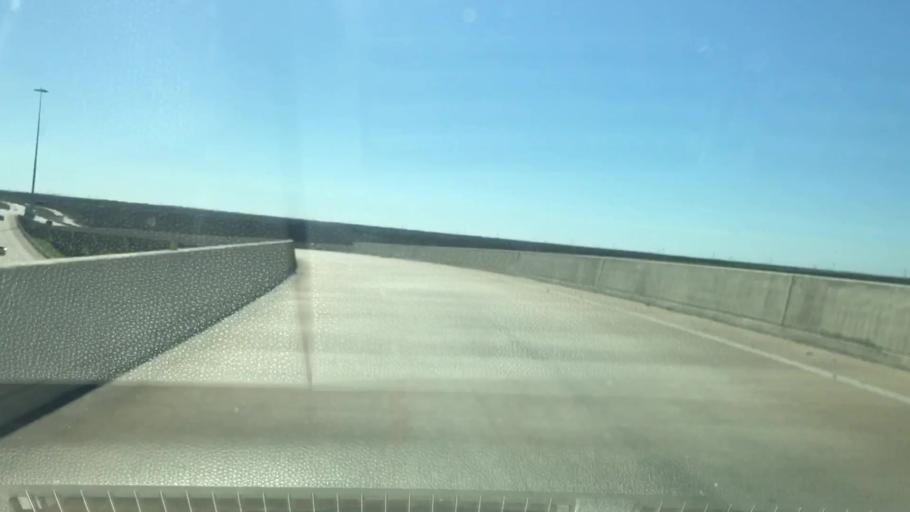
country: US
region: Texas
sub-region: Harris County
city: Cypress
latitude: 29.9968
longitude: -95.7690
